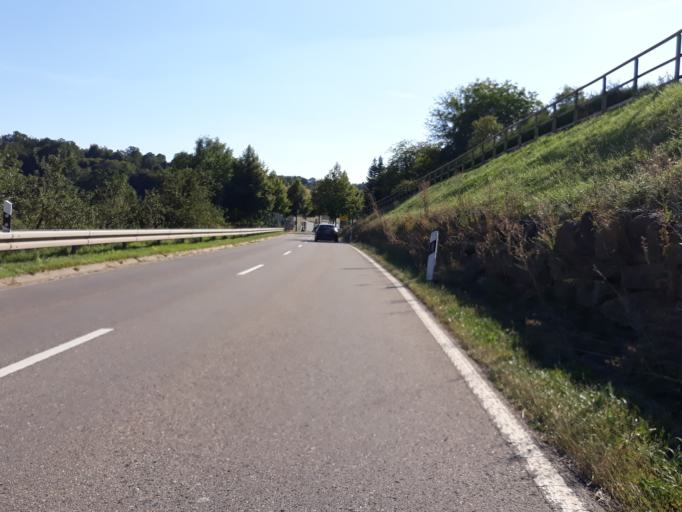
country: DE
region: Baden-Wuerttemberg
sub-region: Karlsruhe Region
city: Gechingen
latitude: 48.6980
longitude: 8.8375
